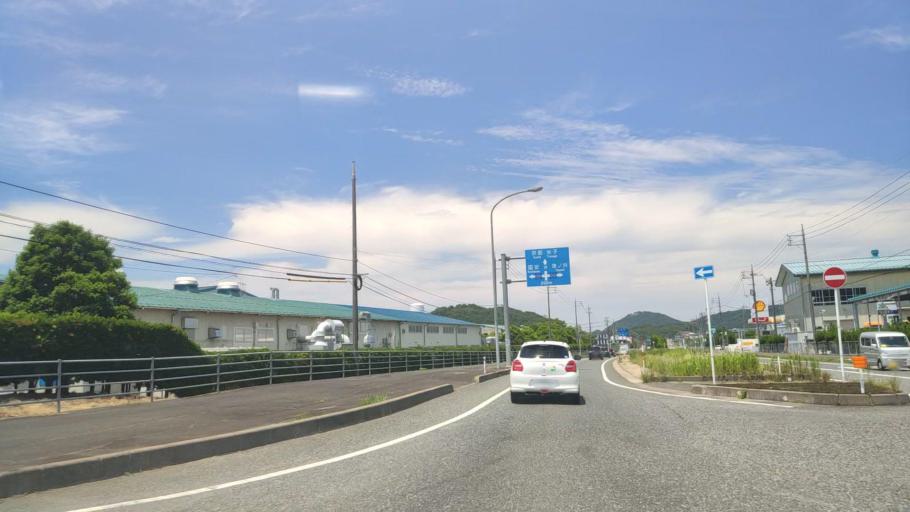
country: JP
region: Tottori
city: Tottori
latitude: 35.4558
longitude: 134.2431
